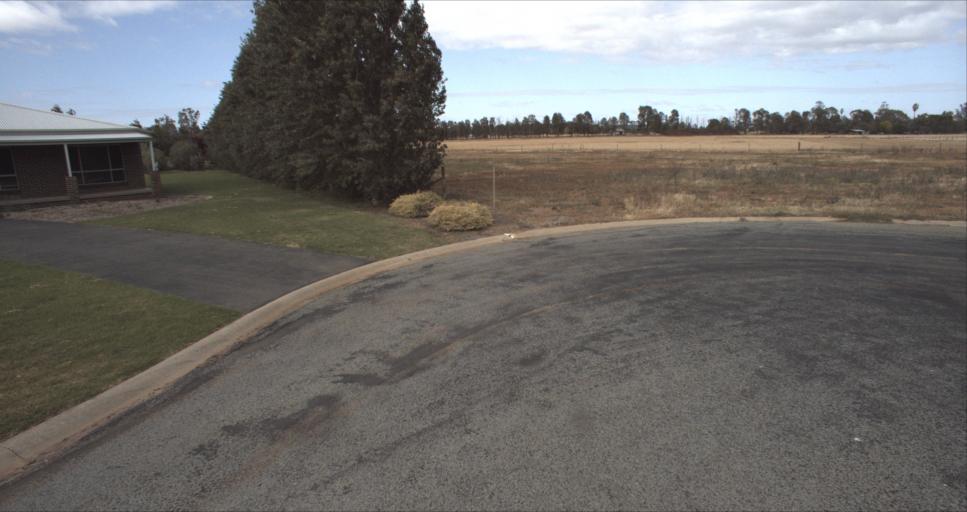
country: AU
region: New South Wales
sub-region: Leeton
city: Leeton
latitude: -34.5595
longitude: 146.4268
